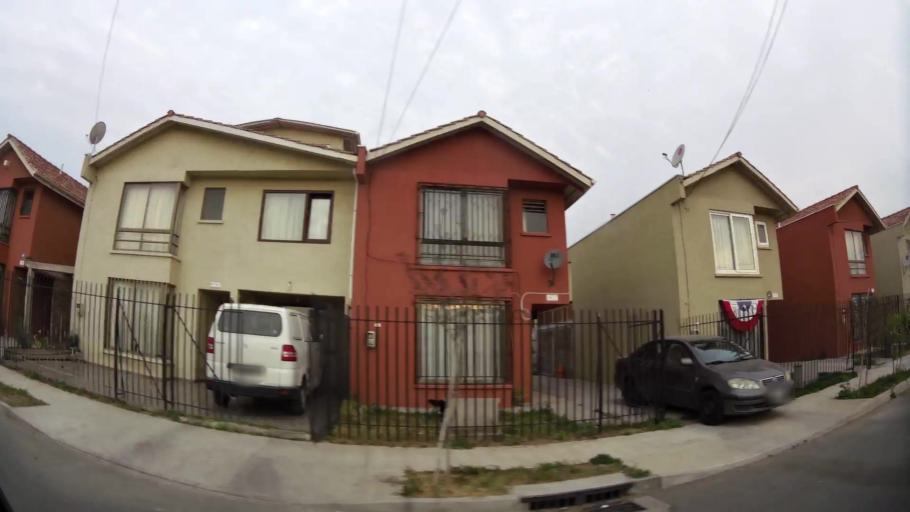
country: CL
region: Santiago Metropolitan
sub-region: Provincia de Talagante
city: Penaflor
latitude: -33.5341
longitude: -70.7999
